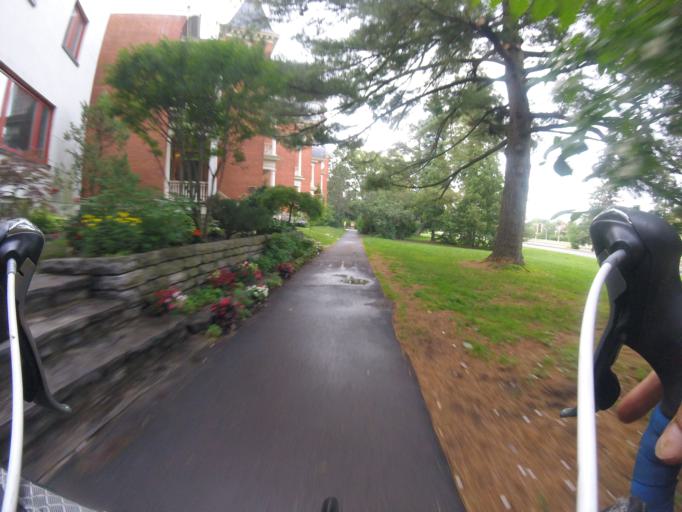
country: CA
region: Ontario
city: Ottawa
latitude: 45.4066
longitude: -75.6824
